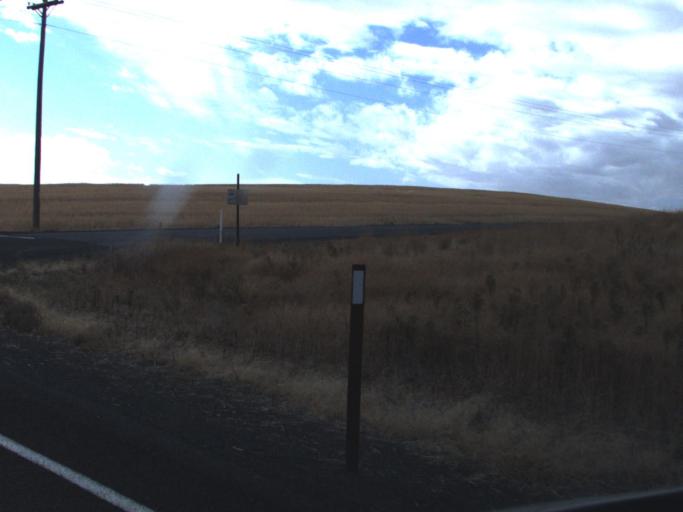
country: US
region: Washington
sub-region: Okanogan County
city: Coulee Dam
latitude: 47.8314
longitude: -118.7217
